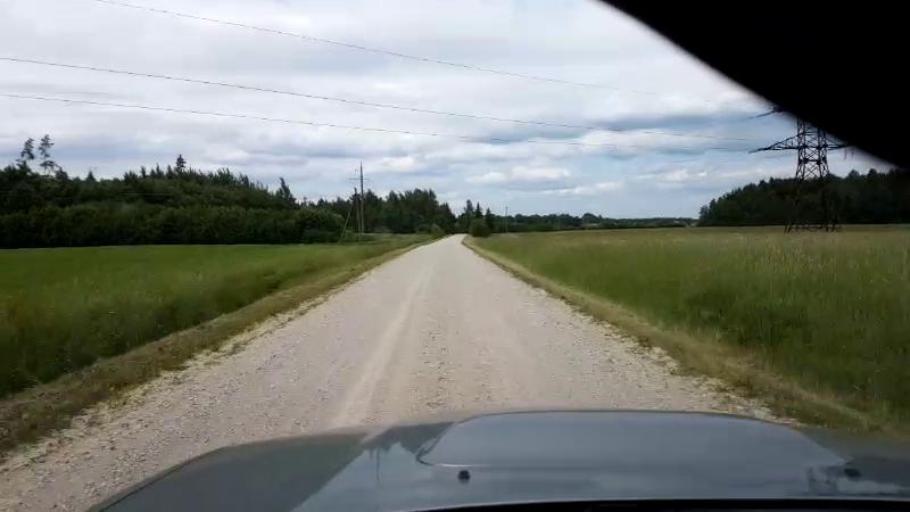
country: EE
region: Paernumaa
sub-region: Halinga vald
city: Parnu-Jaagupi
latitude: 58.5214
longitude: 24.5870
